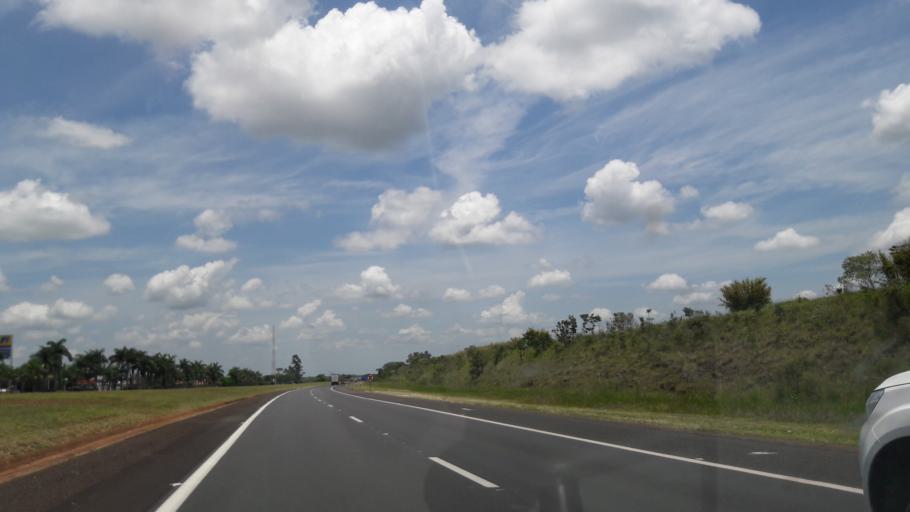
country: BR
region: Sao Paulo
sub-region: Avare
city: Avare
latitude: -22.9567
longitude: -48.8618
